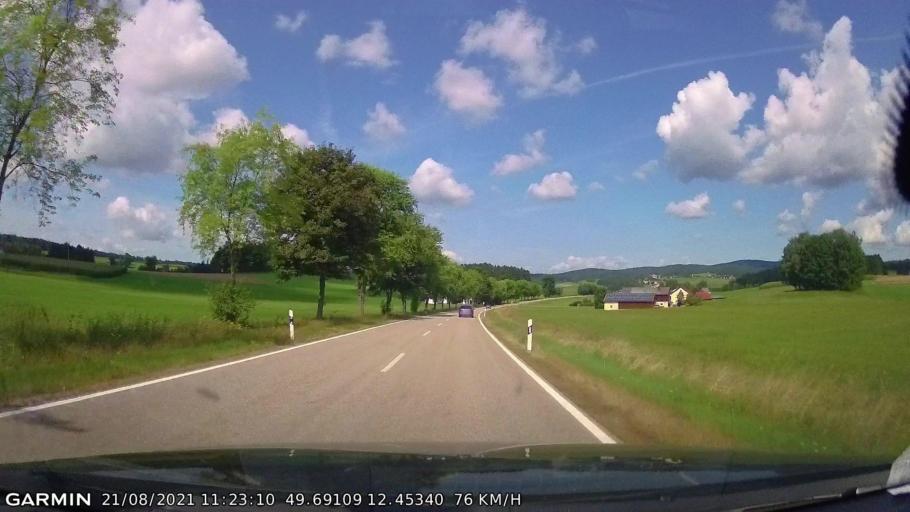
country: DE
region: Bavaria
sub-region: Upper Palatinate
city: Georgenberg
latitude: 49.6911
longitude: 12.4535
